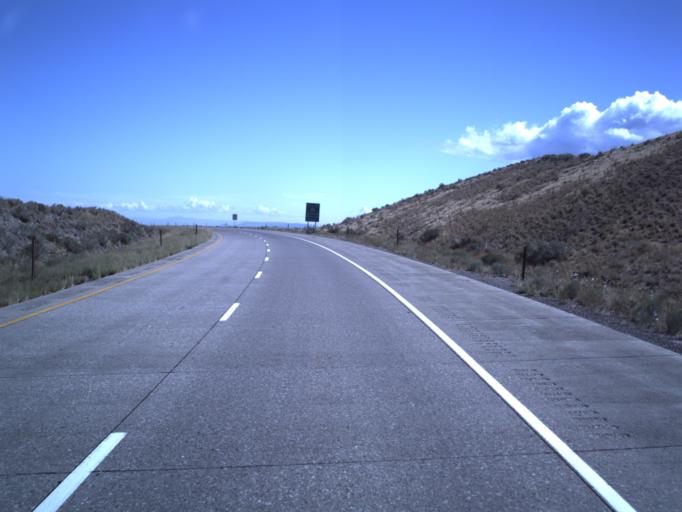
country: US
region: Utah
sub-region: Sevier County
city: Monroe
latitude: 38.6042
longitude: -112.2369
